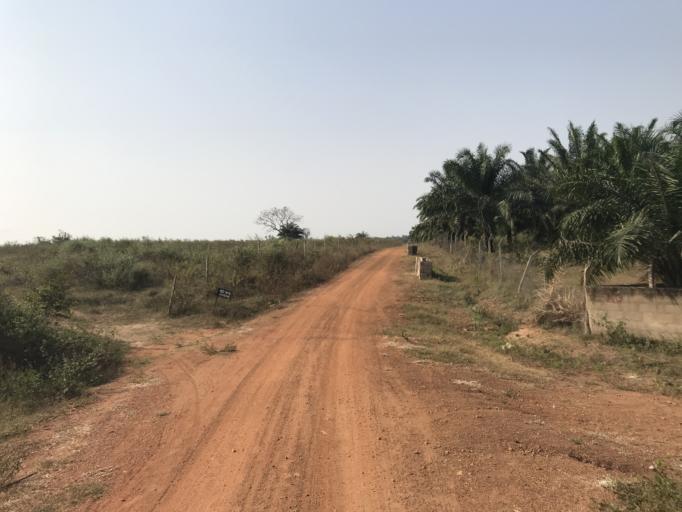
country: NG
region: Osun
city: Olupona
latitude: 7.6013
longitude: 4.1407
